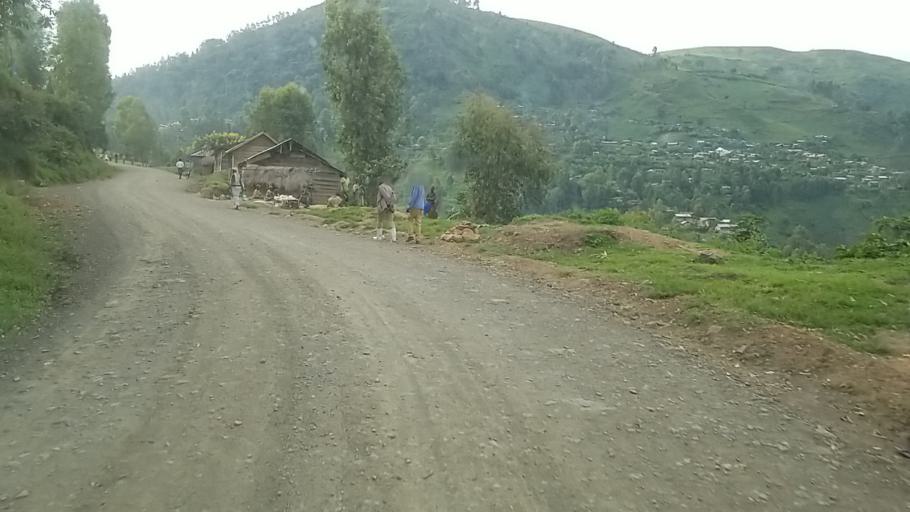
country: CD
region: Nord Kivu
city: Sake
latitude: -1.9229
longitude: 28.9450
